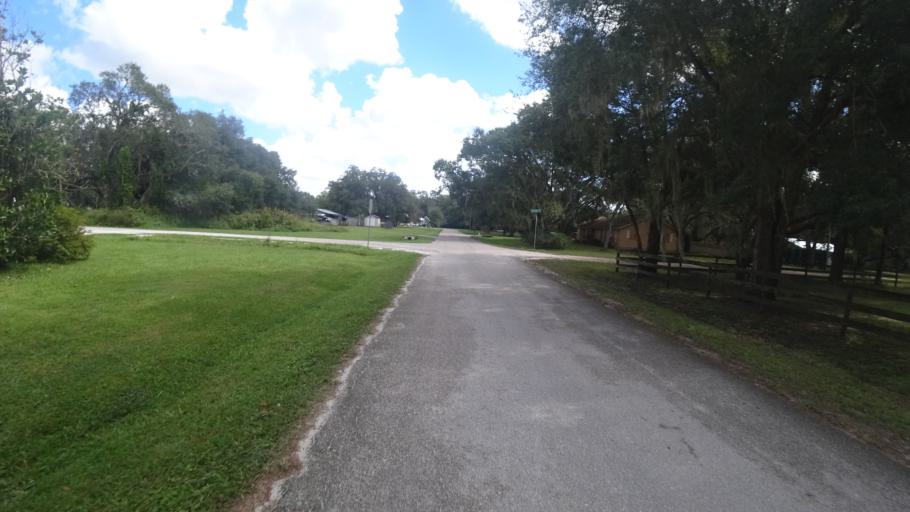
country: US
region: Florida
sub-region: Sarasota County
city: Lake Sarasota
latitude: 27.3492
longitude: -82.1608
